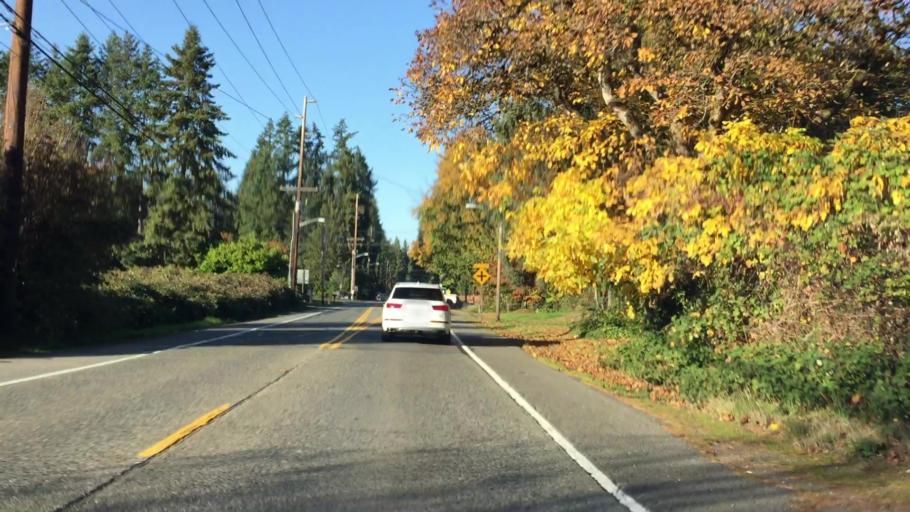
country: US
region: Washington
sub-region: King County
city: Cottage Lake
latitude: 47.7415
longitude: -122.0806
